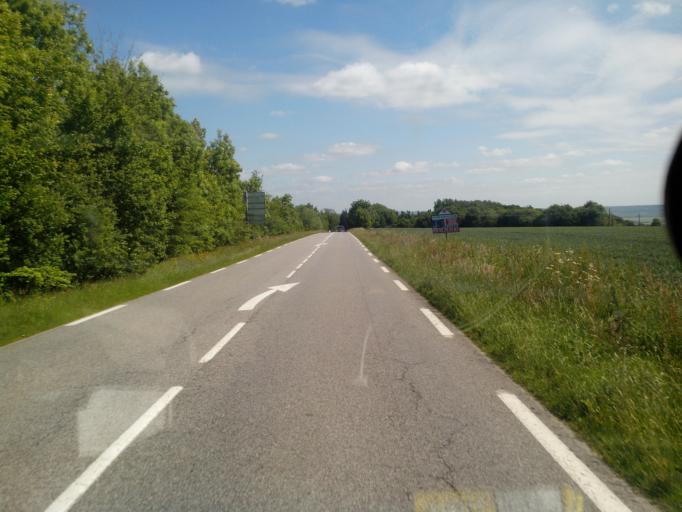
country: FR
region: Haute-Normandie
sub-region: Departement de la Seine-Maritime
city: Tancarville
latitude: 49.4947
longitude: 0.4384
